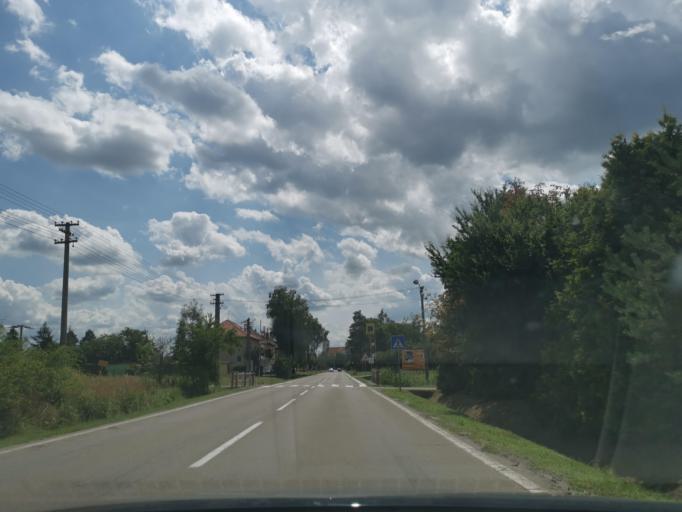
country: CZ
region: South Moravian
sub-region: Okres Breclav
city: Lanzhot
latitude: 48.6642
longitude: 17.0207
